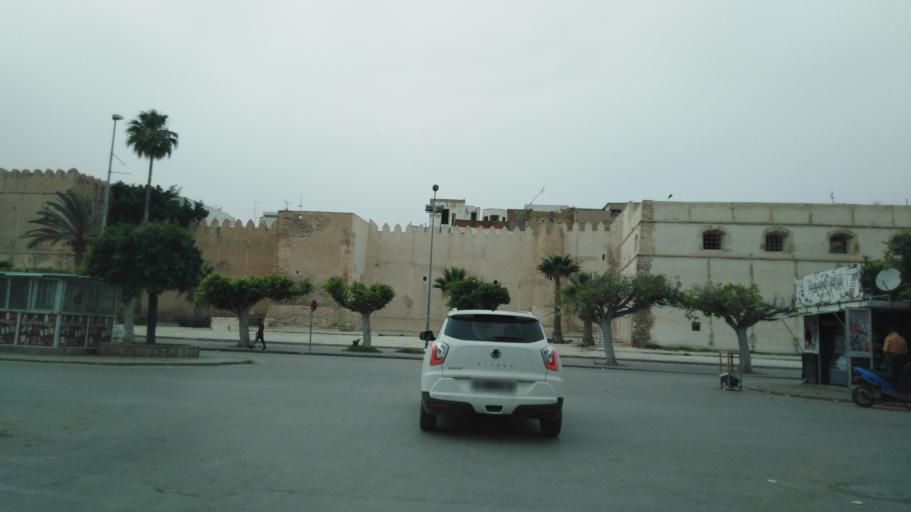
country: TN
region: Safaqis
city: Sfax
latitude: 34.7336
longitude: 10.7612
